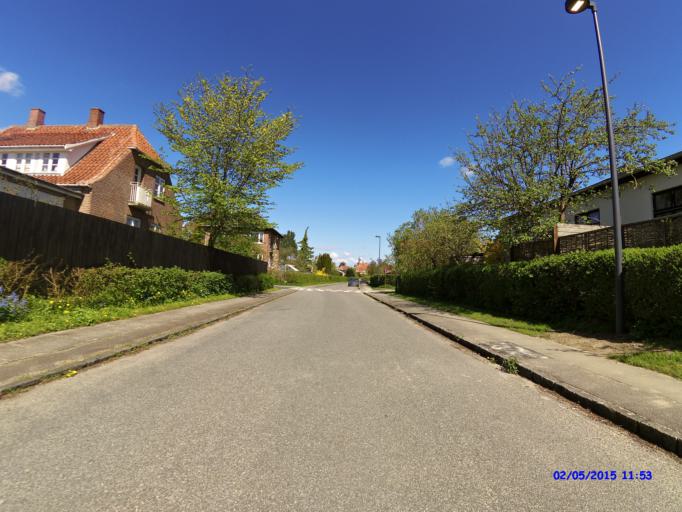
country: DK
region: Capital Region
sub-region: Frederiksberg Kommune
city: Frederiksberg
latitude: 55.7232
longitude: 12.5251
